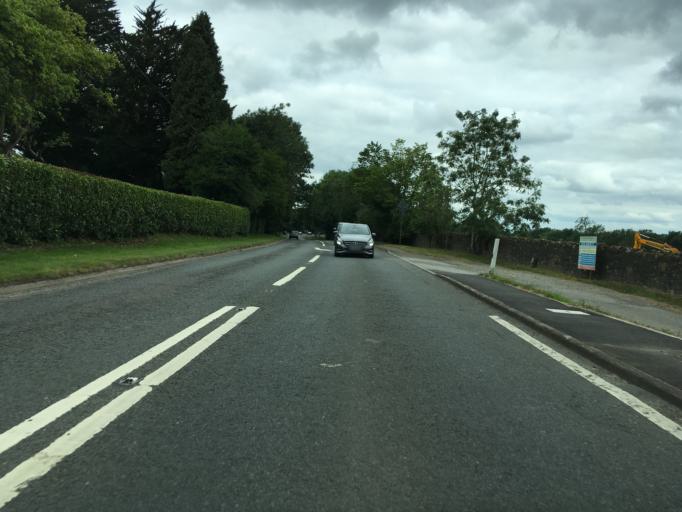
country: GB
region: England
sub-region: Gloucestershire
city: Charlton Kings
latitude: 51.8763
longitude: -2.0240
